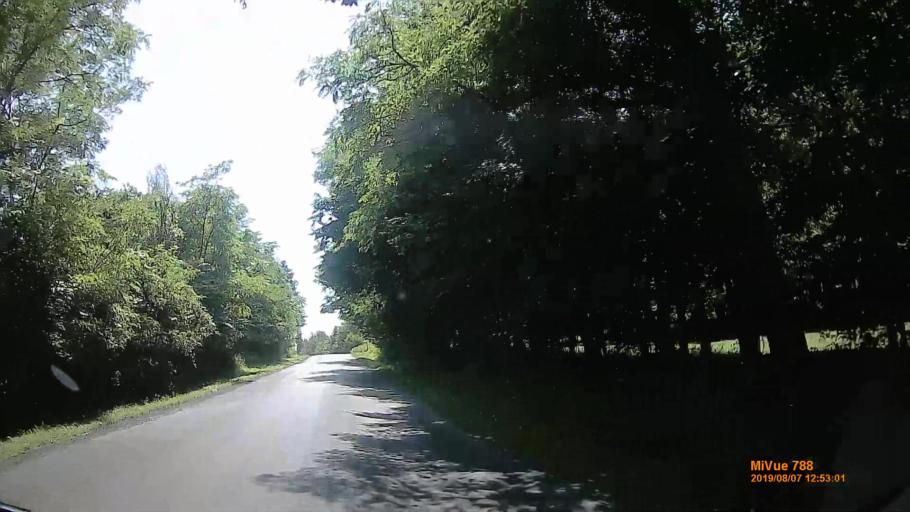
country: HU
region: Zala
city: Cserszegtomaj
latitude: 46.8412
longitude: 17.2679
